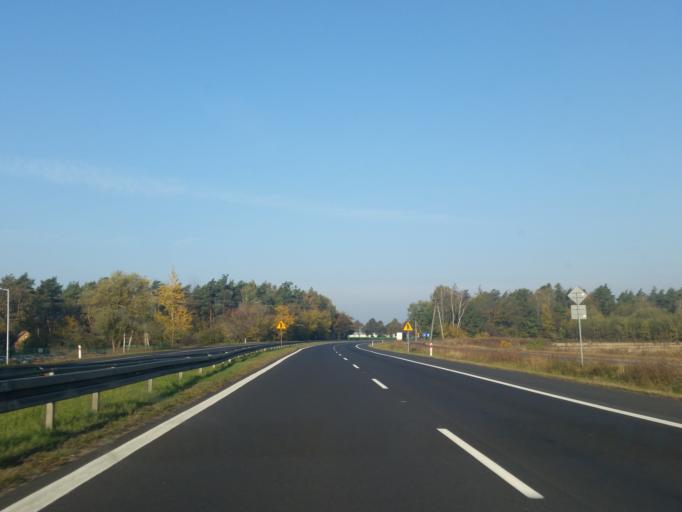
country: PL
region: Masovian Voivodeship
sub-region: Powiat nowodworski
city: Zakroczym
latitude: 52.4521
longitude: 20.5872
